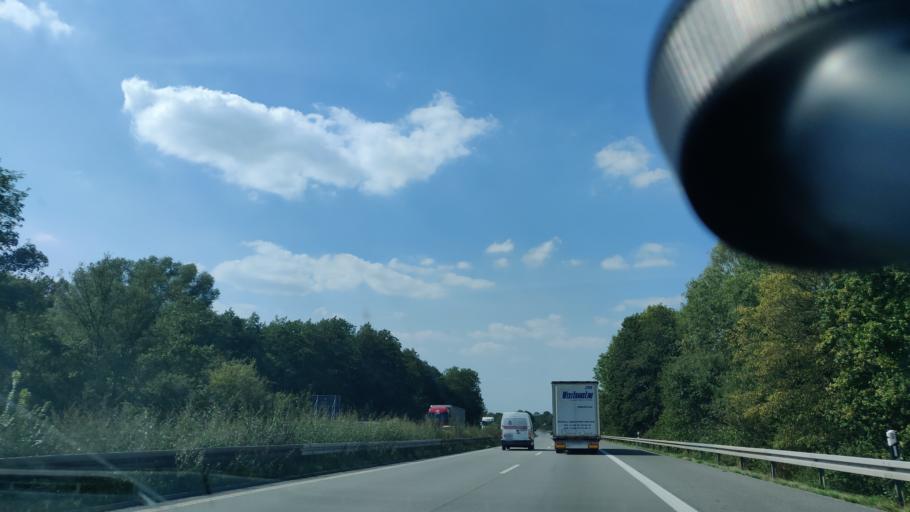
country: DE
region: North Rhine-Westphalia
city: Ibbenburen
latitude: 52.2585
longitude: 7.7670
